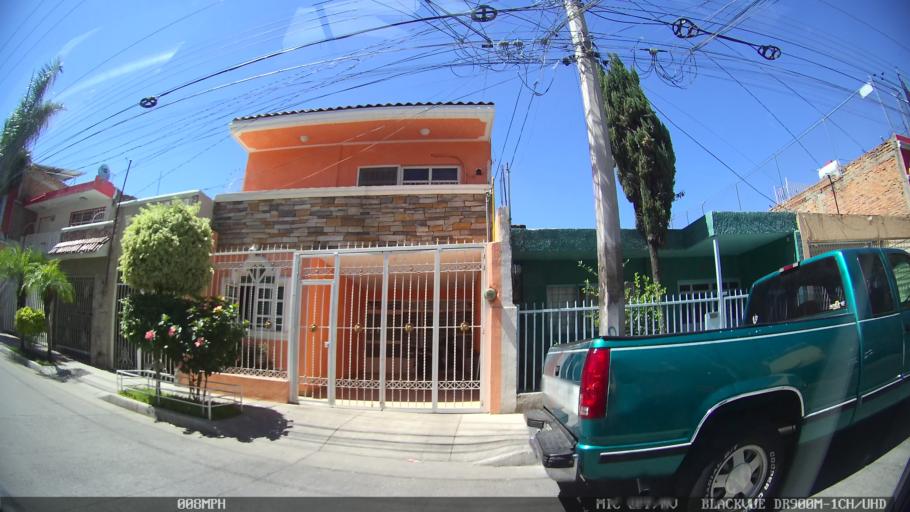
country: MX
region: Jalisco
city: Tlaquepaque
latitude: 20.6651
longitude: -103.2749
